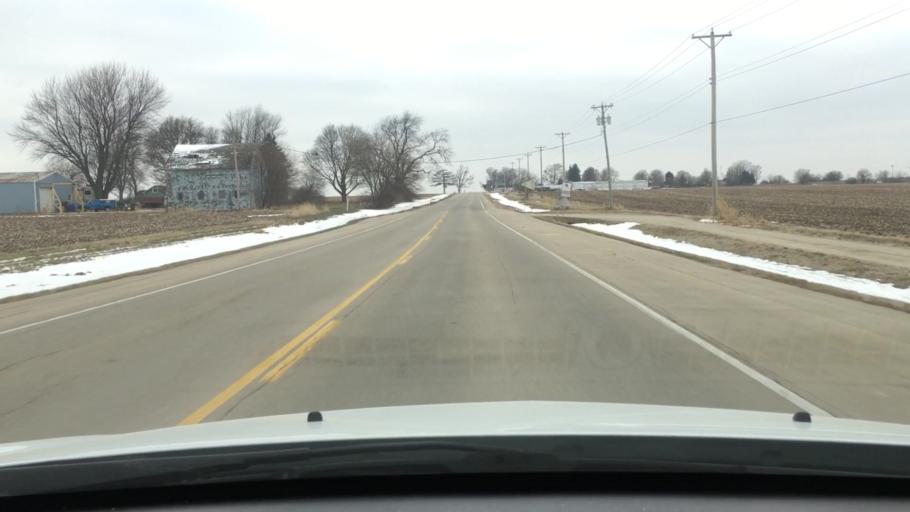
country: US
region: Illinois
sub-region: Ogle County
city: Rochelle
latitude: 41.8980
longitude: -89.0459
